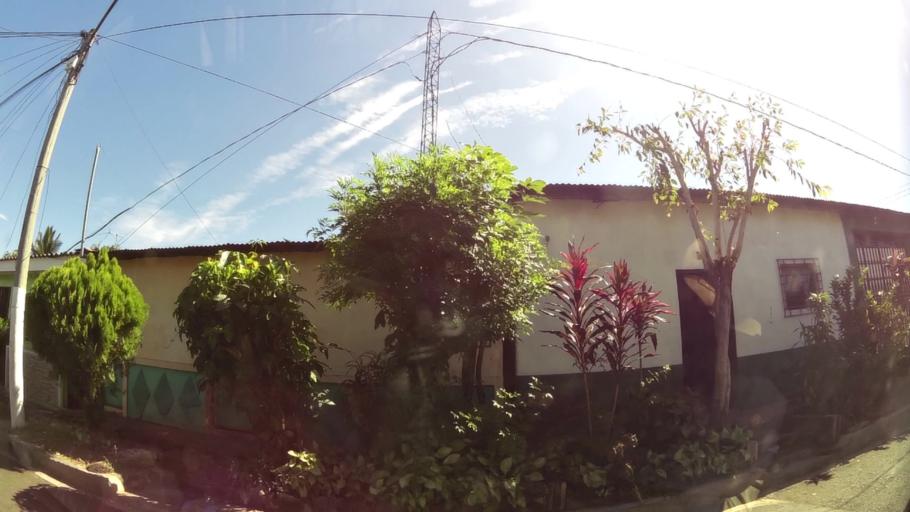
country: SV
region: Ahuachapan
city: Ahuachapan
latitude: 13.9194
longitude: -89.8545
